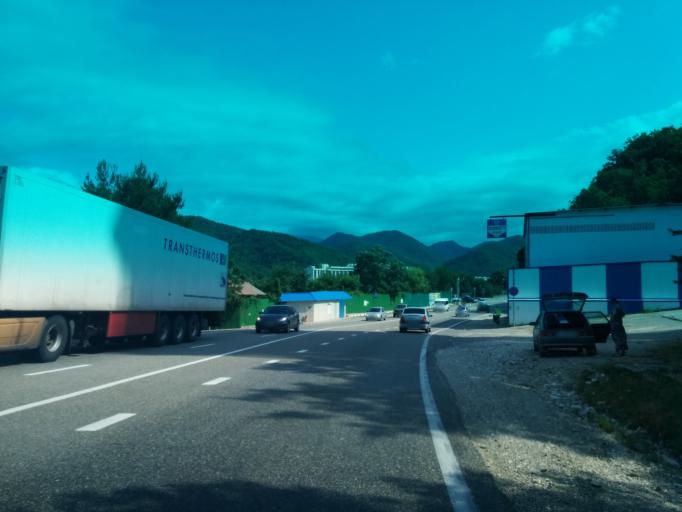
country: RU
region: Krasnodarskiy
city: Nebug
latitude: 44.1613
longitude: 39.0011
